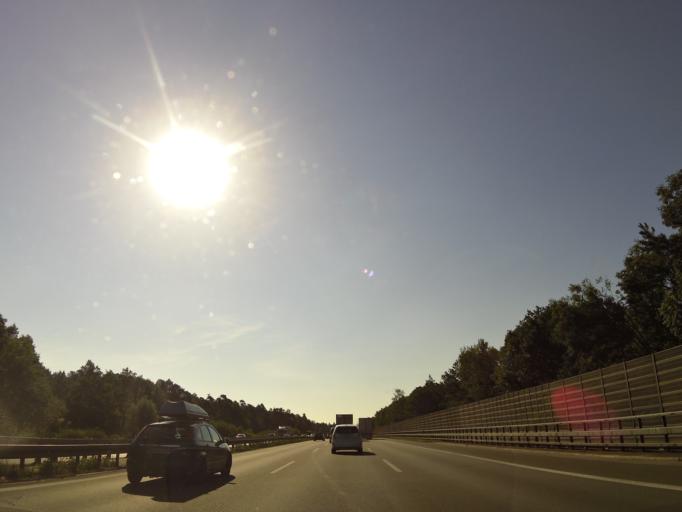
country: DE
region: Bavaria
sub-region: Regierungsbezirk Mittelfranken
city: Heroldsberg
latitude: 49.5089
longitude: 11.1087
